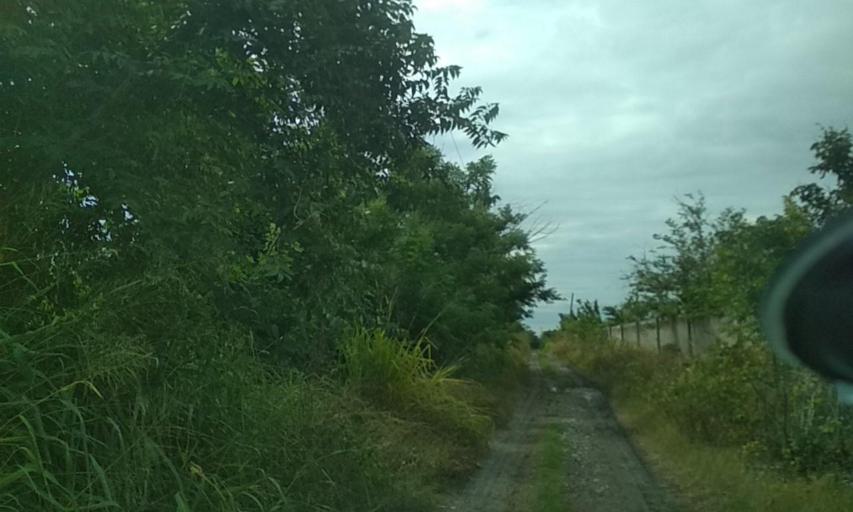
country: MX
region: Veracruz
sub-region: Cazones de Herrera
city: Rancho Nuevo
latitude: 20.6050
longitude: -97.1405
